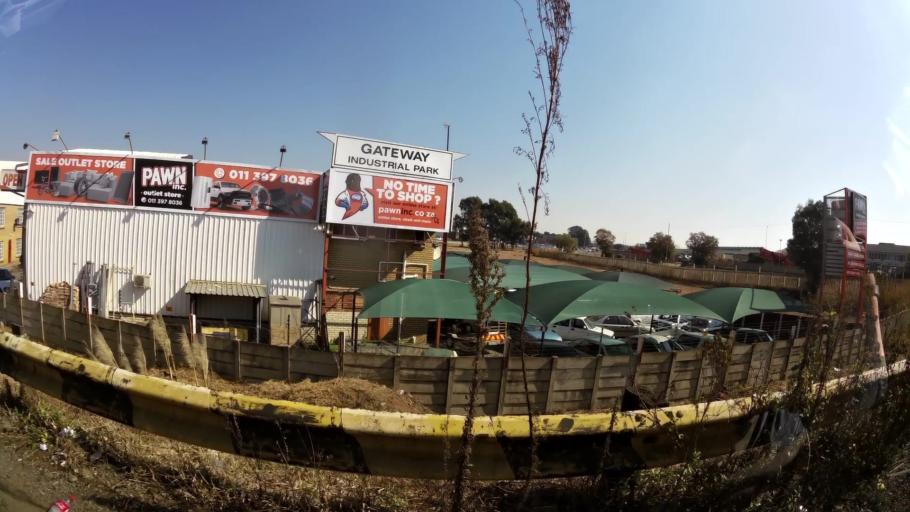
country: ZA
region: Gauteng
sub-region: Ekurhuleni Metropolitan Municipality
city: Boksburg
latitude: -26.1552
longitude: 28.2203
